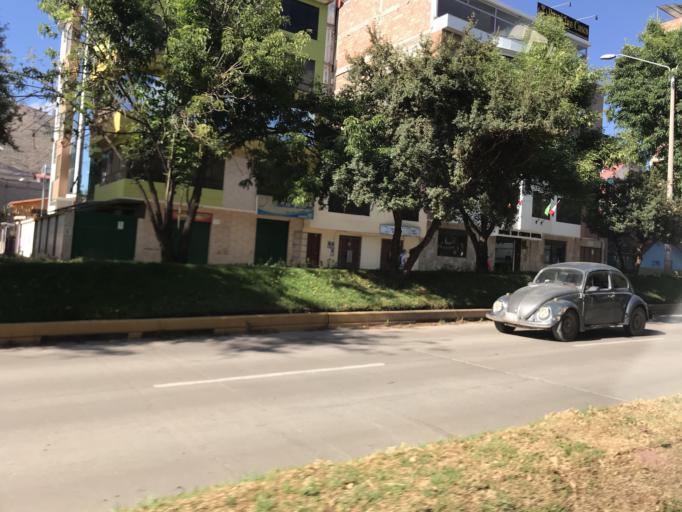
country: PE
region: Cusco
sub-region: Provincia de Cusco
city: Cusco
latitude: -13.5324
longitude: -71.9626
